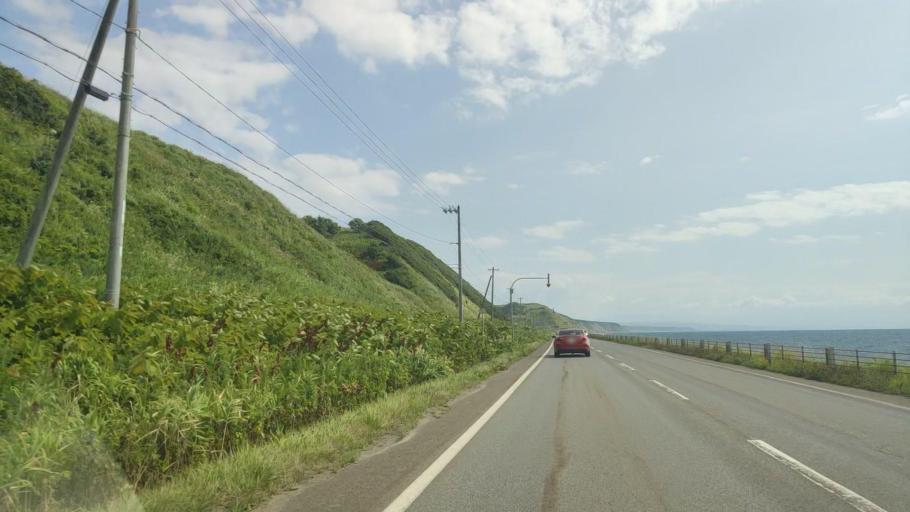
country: JP
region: Hokkaido
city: Rumoi
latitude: 44.0805
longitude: 141.6622
